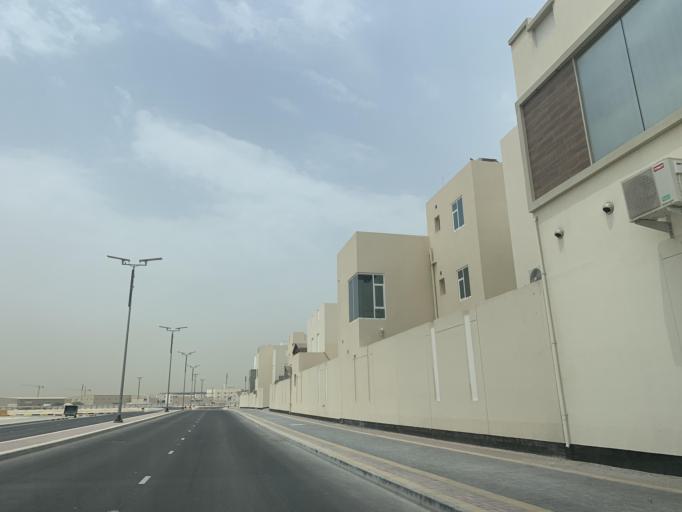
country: BH
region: Northern
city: Madinat `Isa
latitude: 26.1746
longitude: 50.5150
